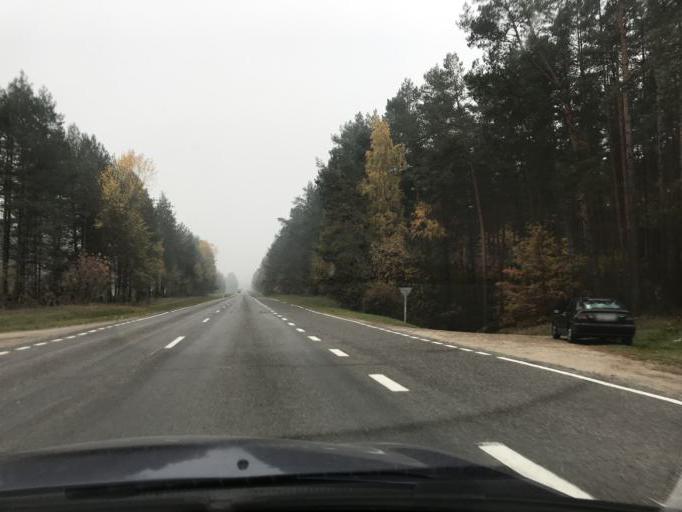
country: BY
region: Grodnenskaya
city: Hrodna
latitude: 53.7962
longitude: 23.8563
